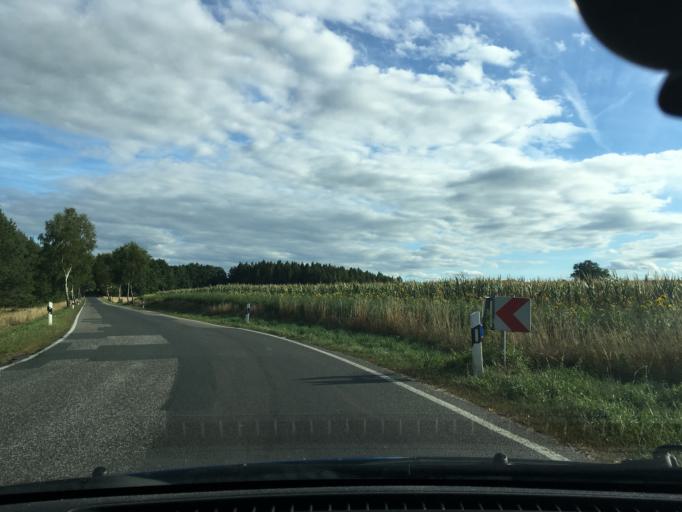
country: DE
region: Lower Saxony
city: Stelle
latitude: 53.3393
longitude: 10.0813
